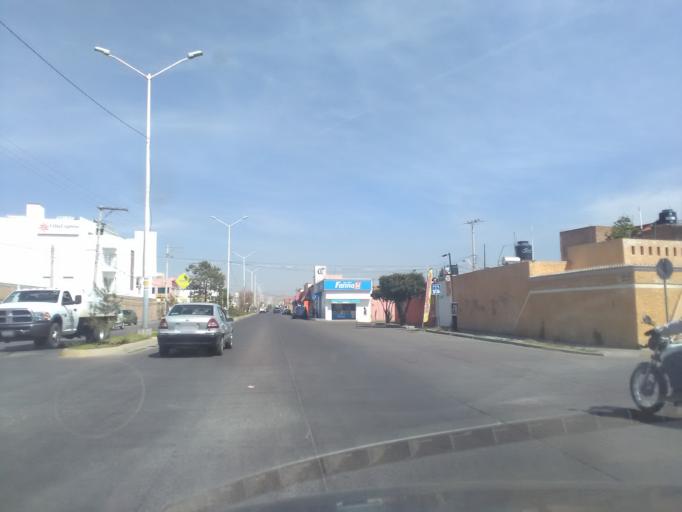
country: MX
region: Durango
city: Victoria de Durango
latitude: 24.0533
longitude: -104.6273
